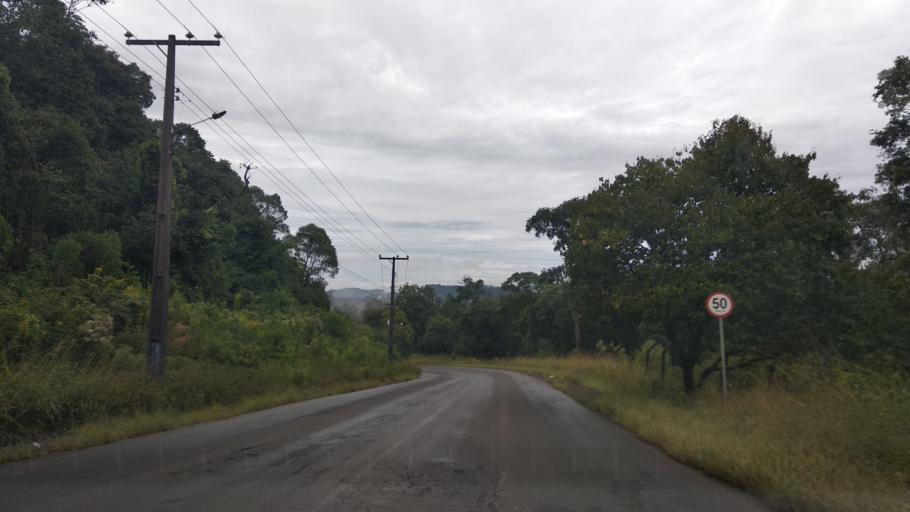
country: BR
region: Santa Catarina
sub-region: Videira
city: Videira
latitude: -26.9959
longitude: -51.1804
